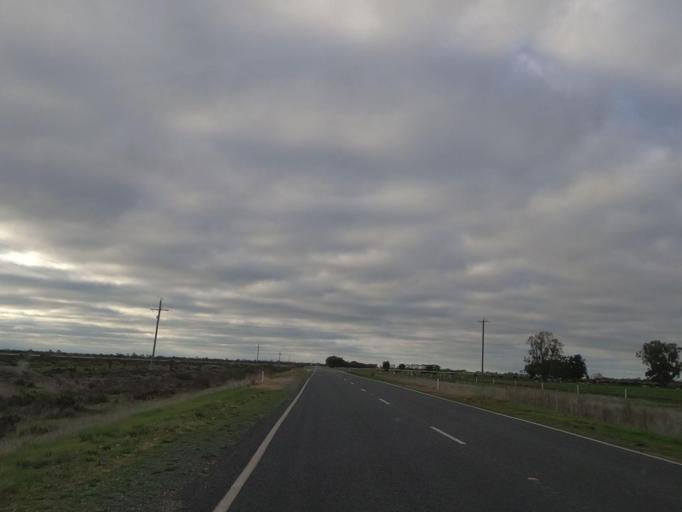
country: AU
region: Victoria
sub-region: Swan Hill
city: Swan Hill
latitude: -35.8357
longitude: 143.9419
